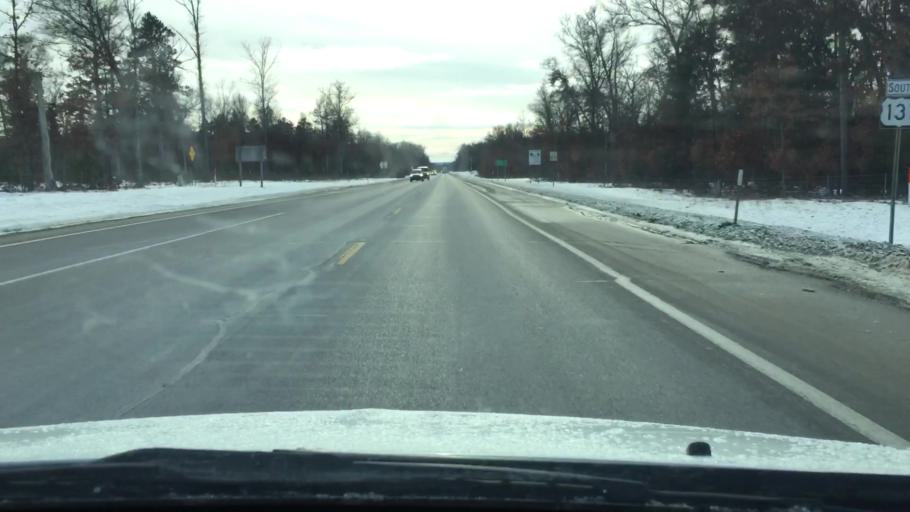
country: US
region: Michigan
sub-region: Wexford County
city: Manton
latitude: 44.5238
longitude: -85.3911
